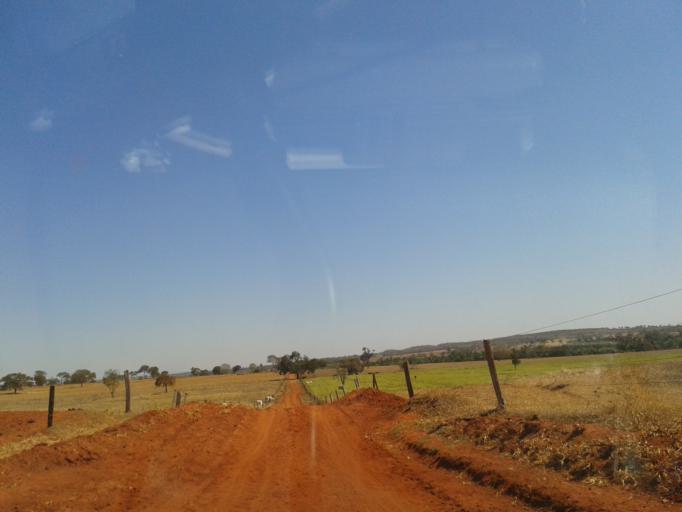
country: BR
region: Minas Gerais
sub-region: Santa Vitoria
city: Santa Vitoria
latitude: -19.0792
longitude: -50.0669
